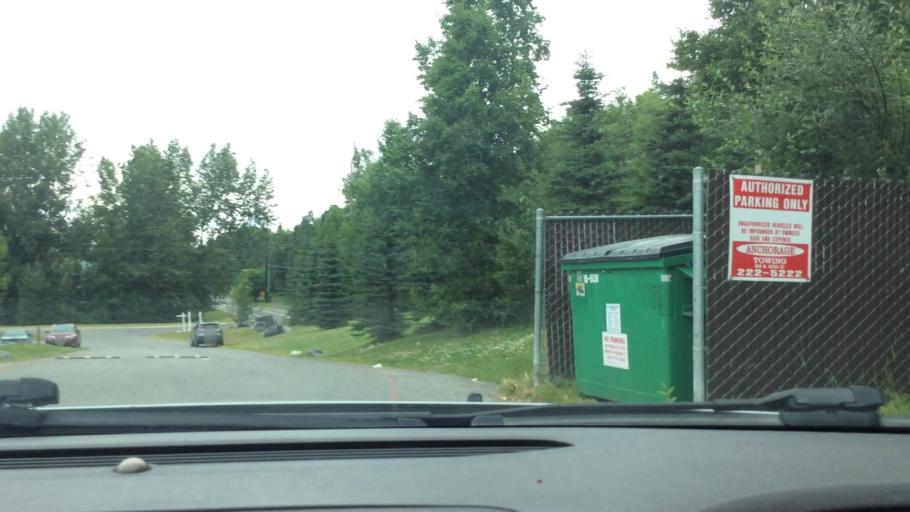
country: US
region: Alaska
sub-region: Anchorage Municipality
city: Anchorage
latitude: 61.2034
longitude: -149.7939
